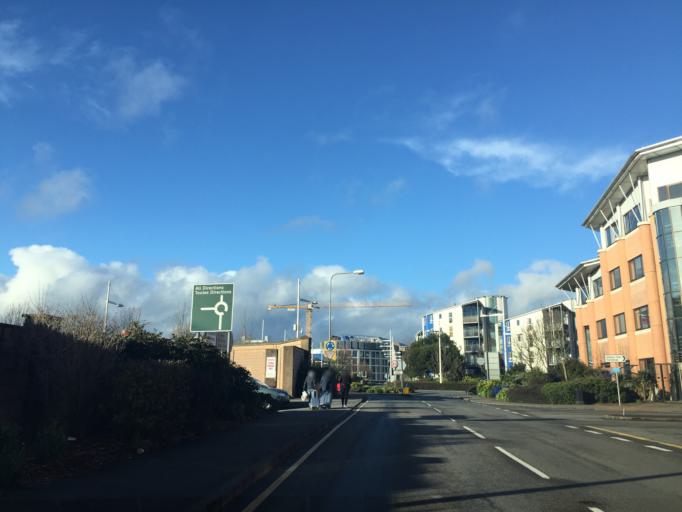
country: JE
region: St Helier
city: Saint Helier
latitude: 49.1813
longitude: -2.1139
